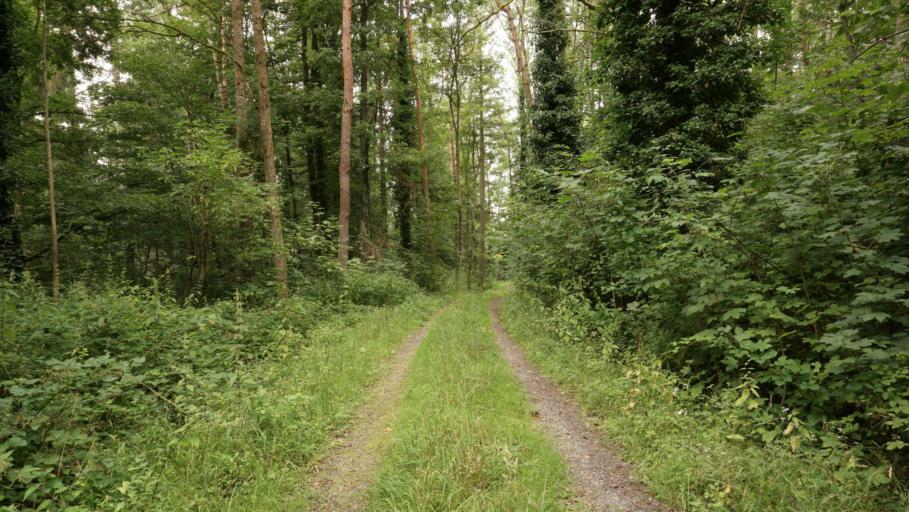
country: DE
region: Baden-Wuerttemberg
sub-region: Karlsruhe Region
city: Hassmersheim
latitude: 49.3153
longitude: 9.1532
